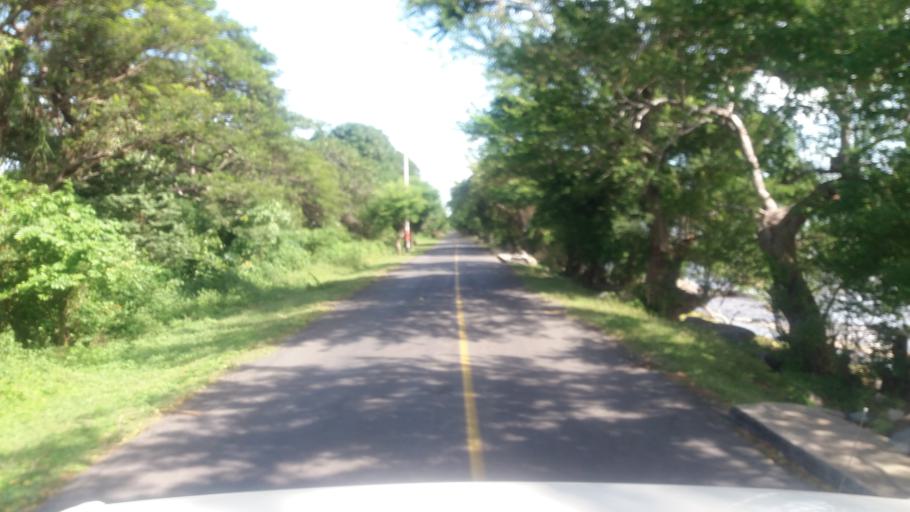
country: NI
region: Granada
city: Granada
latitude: 11.9765
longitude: -85.9420
